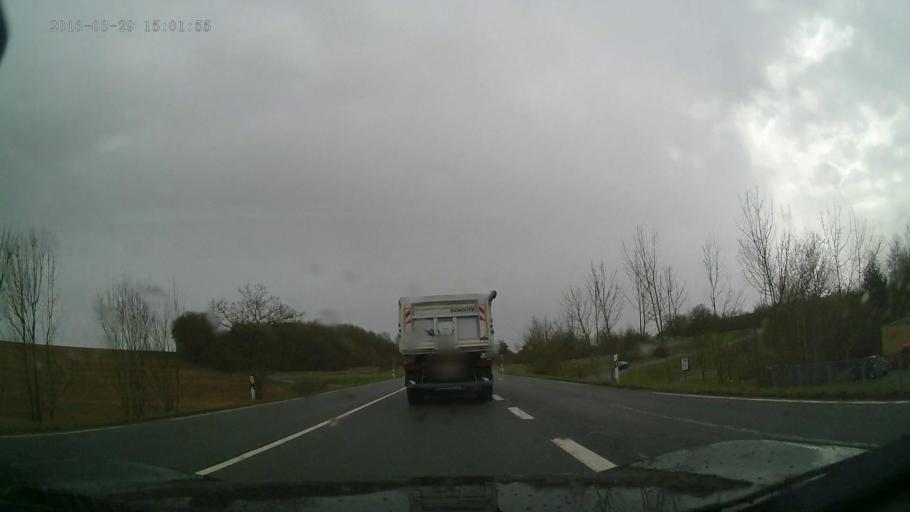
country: DE
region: Baden-Wuerttemberg
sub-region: Karlsruhe Region
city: Walldurn
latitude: 49.5654
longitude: 9.3626
